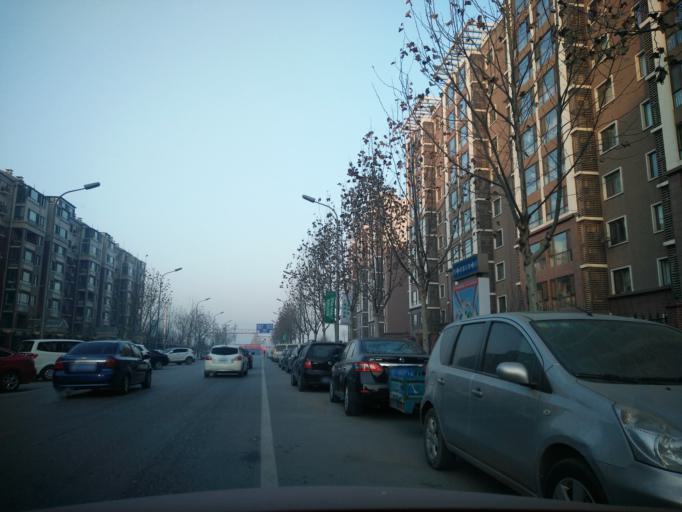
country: CN
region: Beijing
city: Xingfeng
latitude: 39.7149
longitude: 116.3934
